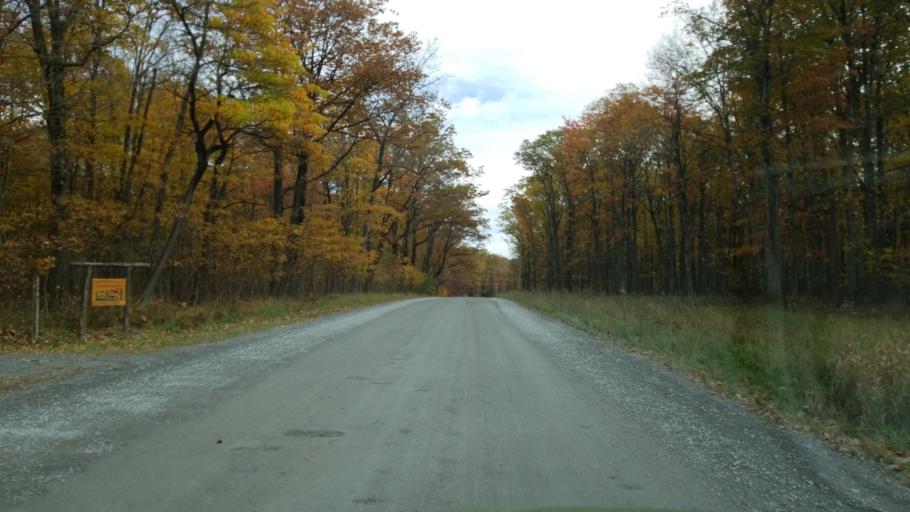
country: US
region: Pennsylvania
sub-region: Clearfield County
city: Clearfield
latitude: 41.1434
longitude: -78.4947
